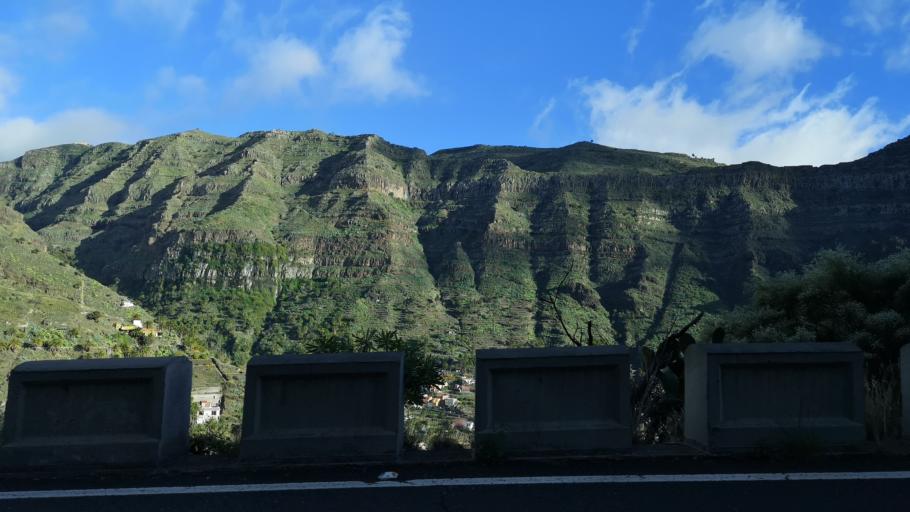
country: ES
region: Canary Islands
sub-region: Provincia de Santa Cruz de Tenerife
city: Vallehermosa
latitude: 28.1197
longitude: -17.3128
